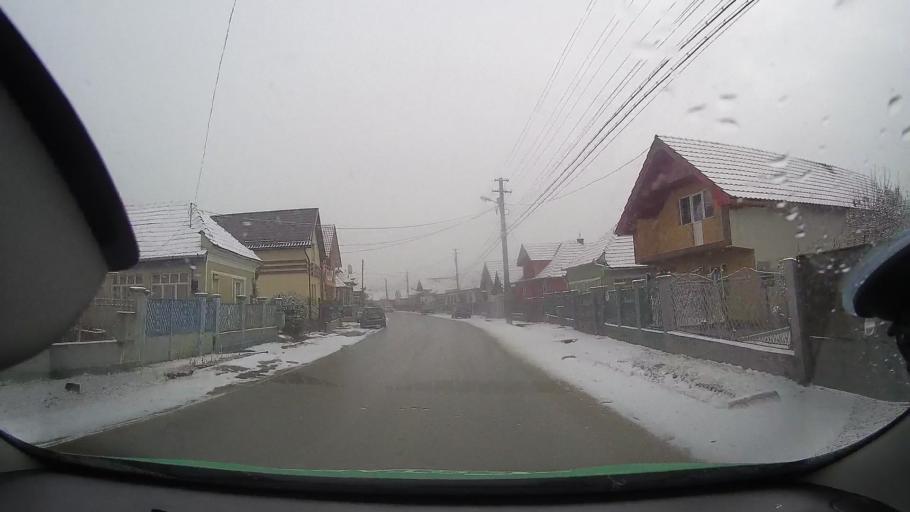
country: RO
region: Alba
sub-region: Municipiul Aiud
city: Ciumbrud
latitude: 46.3077
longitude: 23.7619
